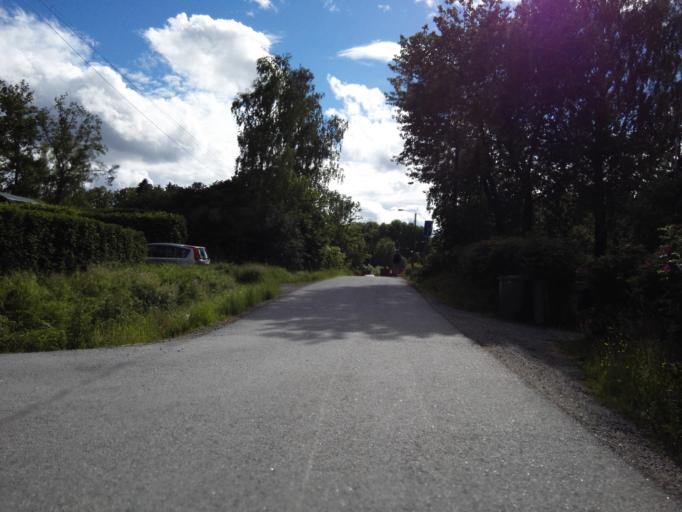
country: SE
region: Stockholm
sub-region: Stockholms Kommun
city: Arsta
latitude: 59.2291
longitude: 18.0838
